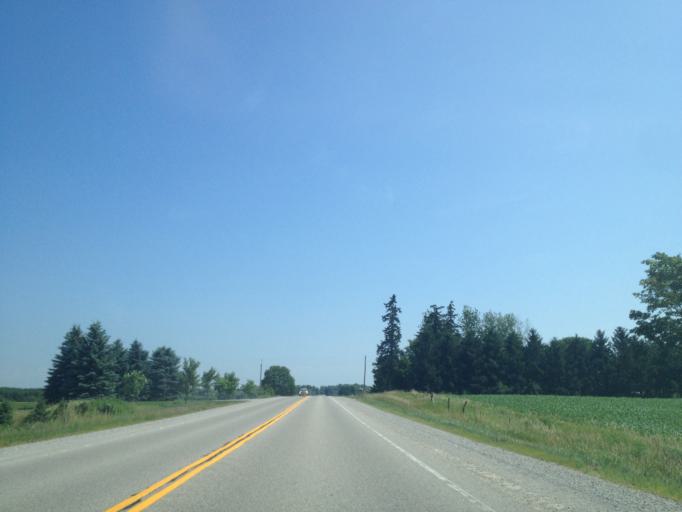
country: CA
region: Ontario
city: London
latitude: 43.2448
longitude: -81.2164
